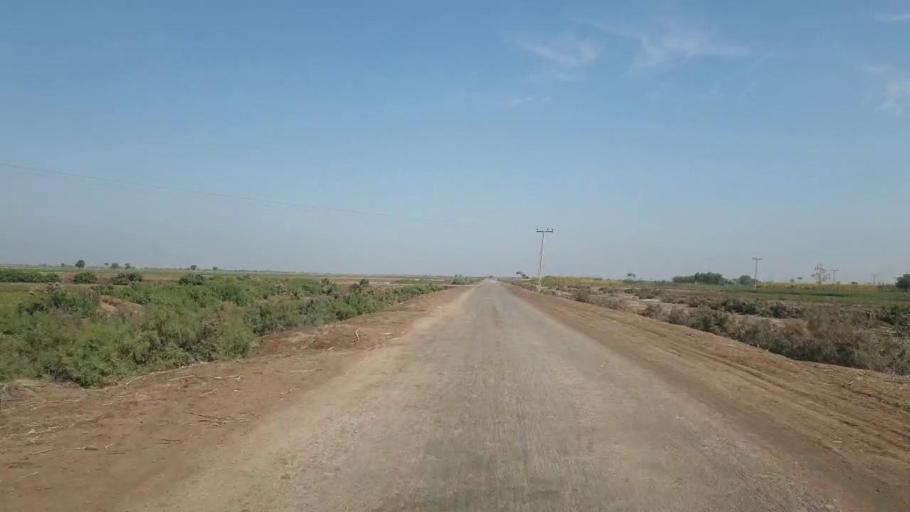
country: PK
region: Sindh
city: Samaro
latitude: 25.3463
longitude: 69.2496
